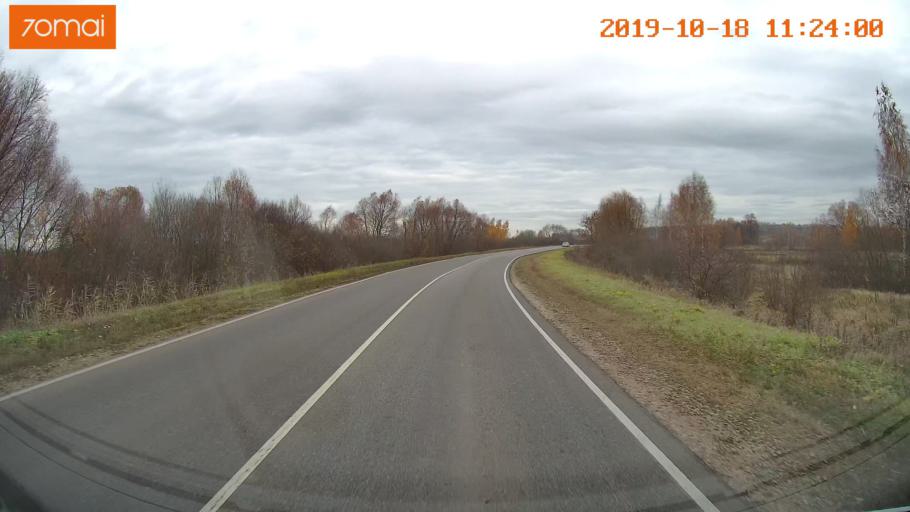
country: RU
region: Tula
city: Kimovsk
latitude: 54.1097
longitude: 38.5951
